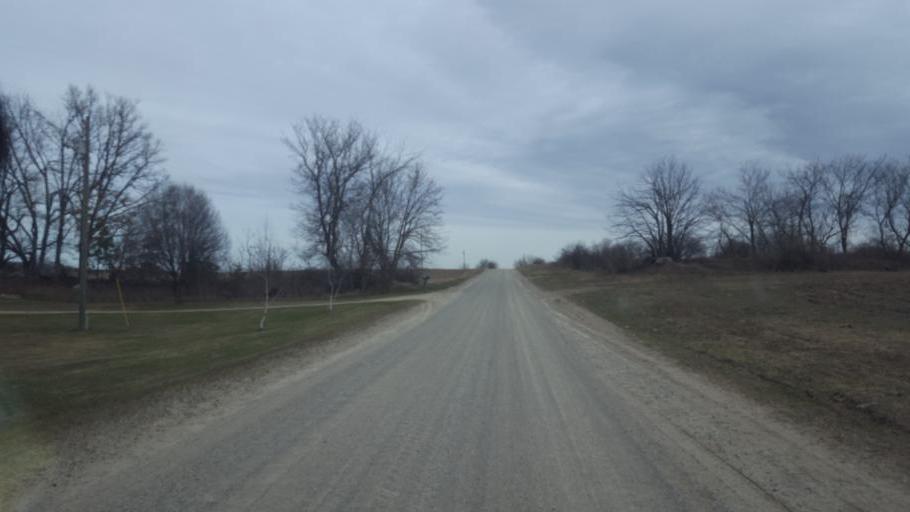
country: US
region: Michigan
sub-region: Montcalm County
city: Edmore
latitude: 43.4513
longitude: -85.0156
